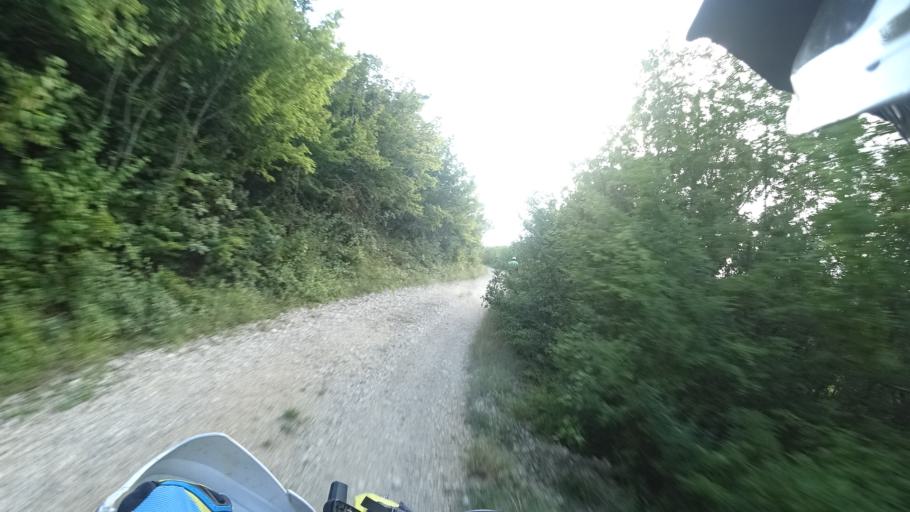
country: HR
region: Sibensko-Kniniska
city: Knin
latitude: 44.1797
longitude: 16.0698
